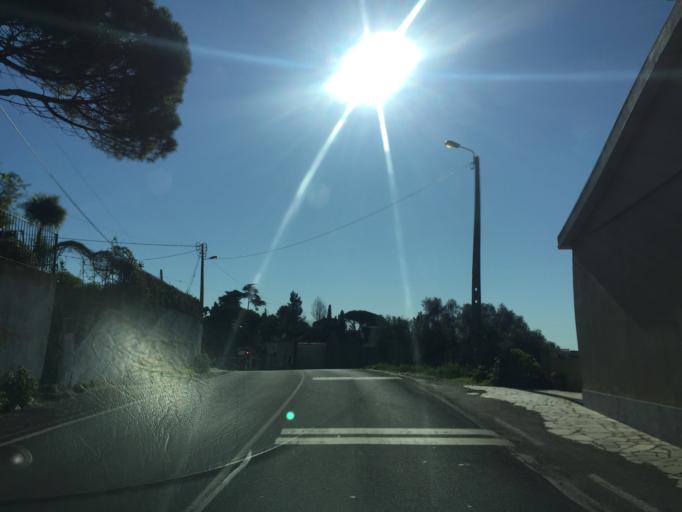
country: PT
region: Lisbon
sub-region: Sintra
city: Pero Pinheiro
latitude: 38.8350
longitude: -9.3096
